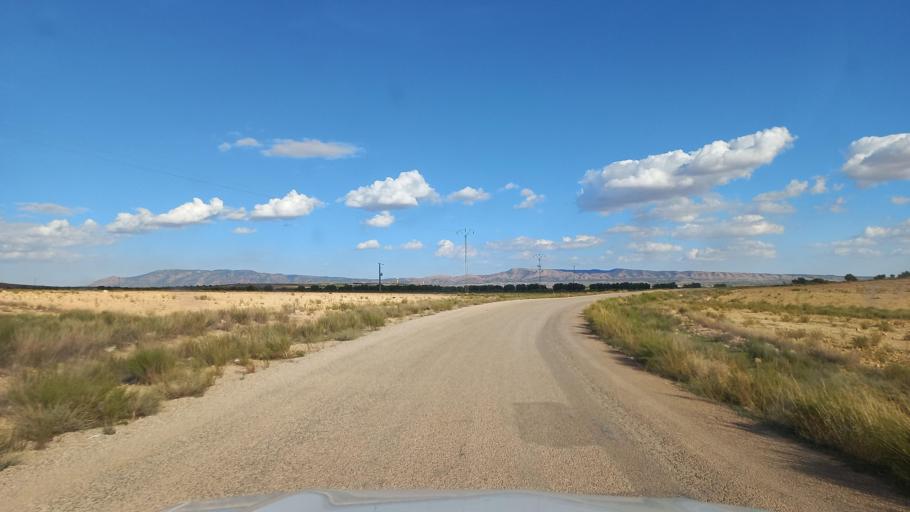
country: TN
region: Al Qasrayn
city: Sbiba
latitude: 35.3923
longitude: 9.0232
